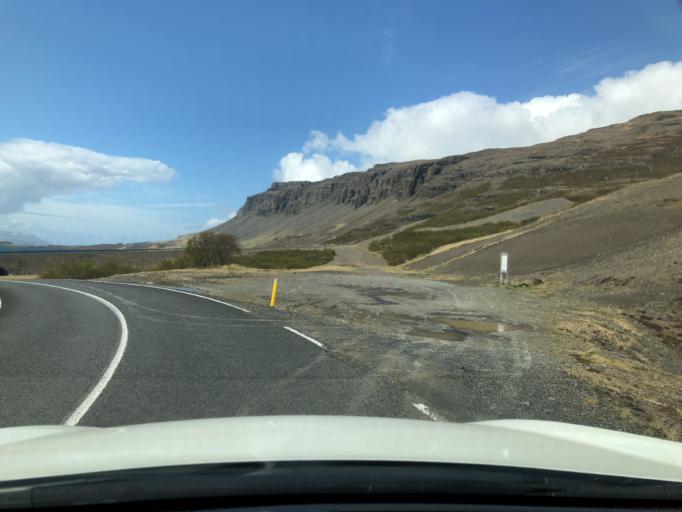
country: IS
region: Capital Region
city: Mosfellsbaer
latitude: 64.3863
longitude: -21.3514
